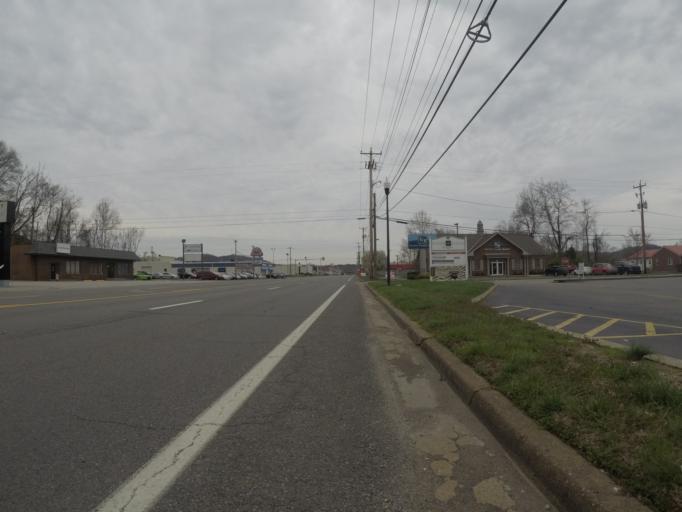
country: US
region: West Virginia
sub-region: Cabell County
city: Pea Ridge
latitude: 38.4133
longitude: -82.3079
